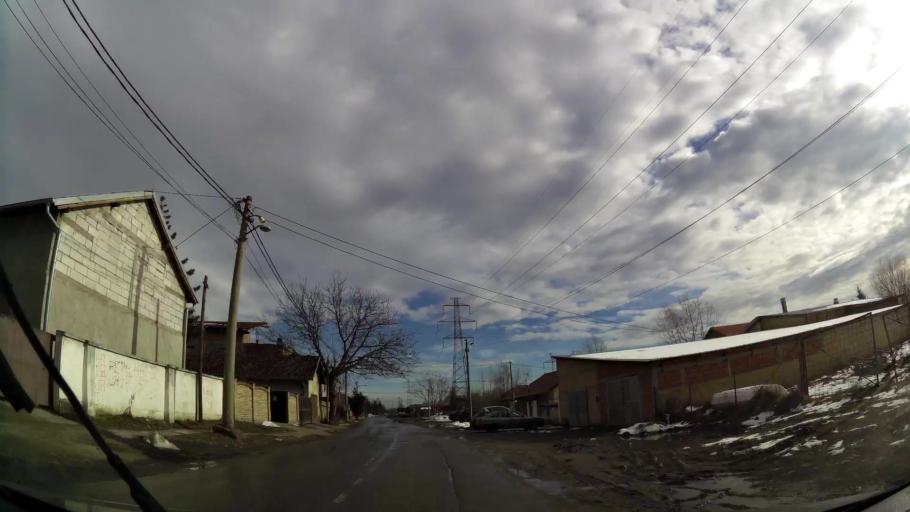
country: RS
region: Central Serbia
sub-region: Belgrade
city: Zemun
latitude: 44.7984
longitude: 20.3518
